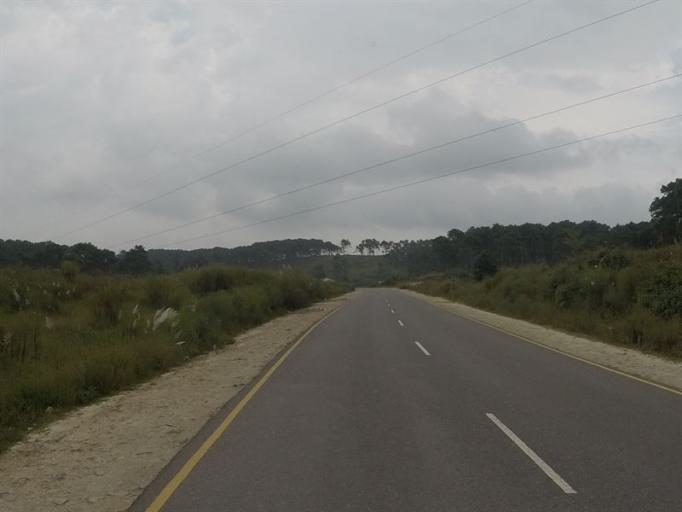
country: IN
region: Meghalaya
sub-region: East Khasi Hills
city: Shillong
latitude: 25.4945
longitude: 92.1740
